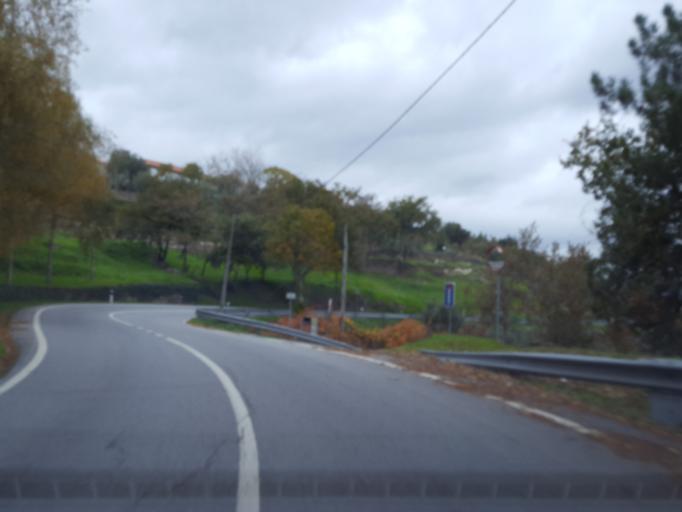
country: PT
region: Porto
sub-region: Marco de Canaveses
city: Marco de Canavezes
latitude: 41.1624
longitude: -8.1456
